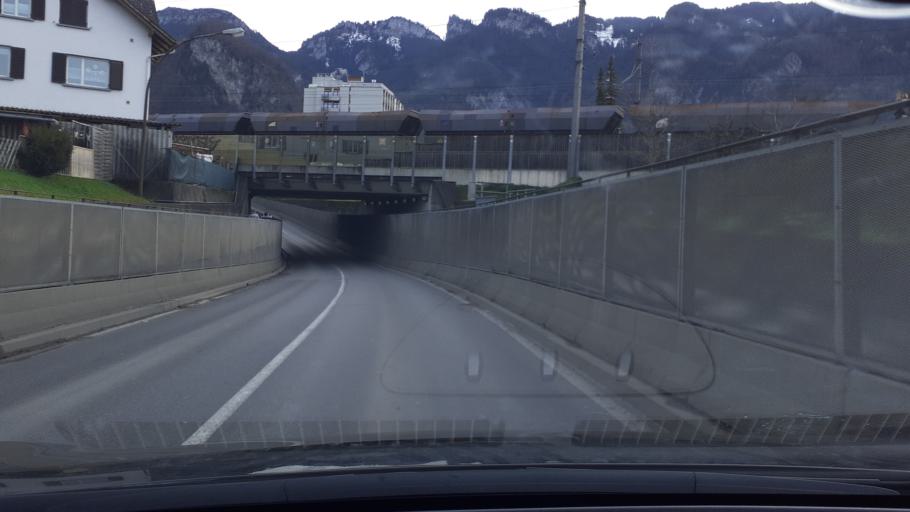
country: AT
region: Vorarlberg
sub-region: Politischer Bezirk Dornbirn
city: Hohenems
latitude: 47.3633
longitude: 9.6781
